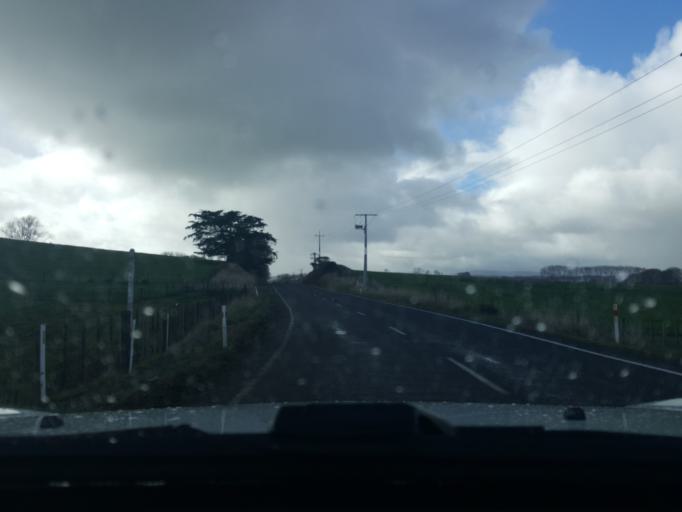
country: NZ
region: Waikato
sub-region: Waikato District
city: Te Kauwhata
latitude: -37.4487
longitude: 175.1037
